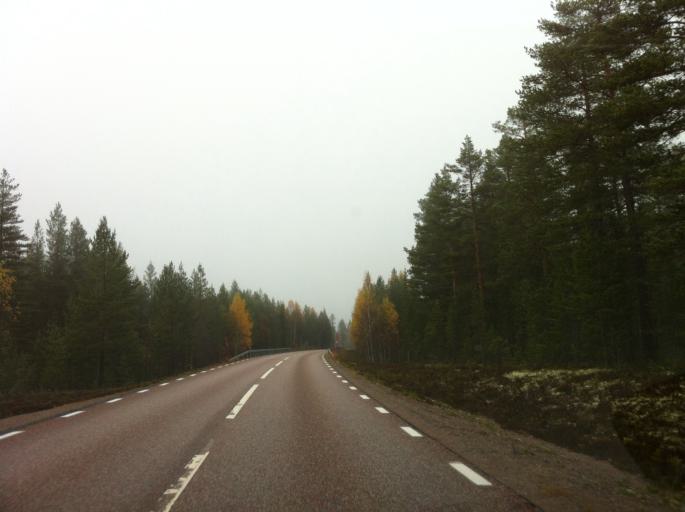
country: NO
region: Hedmark
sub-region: Trysil
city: Innbygda
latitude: 61.7455
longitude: 12.9729
